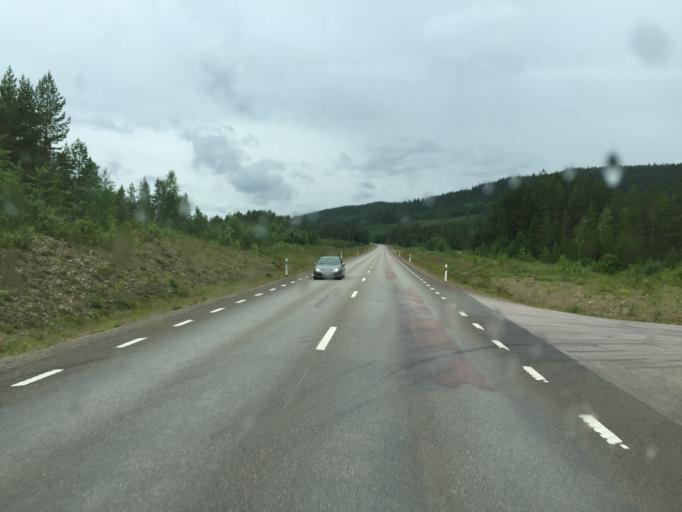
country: SE
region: Dalarna
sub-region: Malung-Saelens kommun
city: Malung
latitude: 60.6436
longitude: 13.6253
